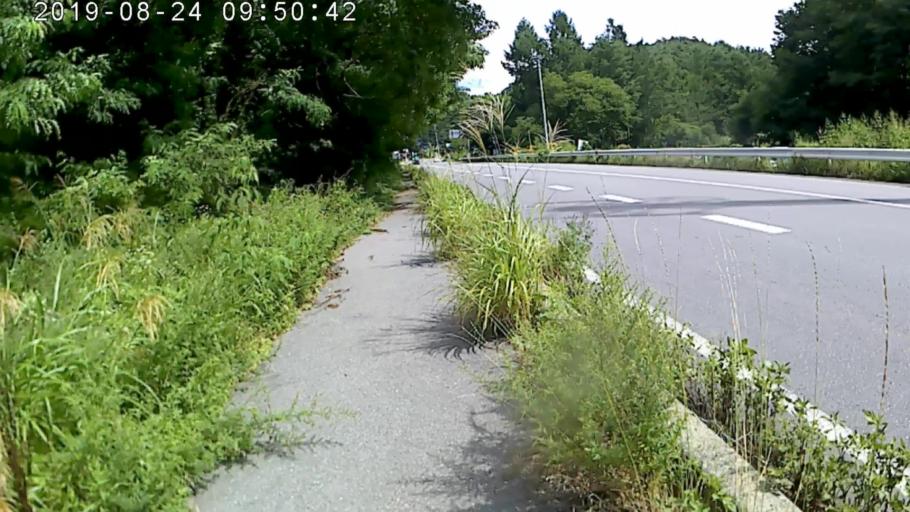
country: JP
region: Nagano
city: Kamimaruko
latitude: 36.2546
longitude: 138.2864
